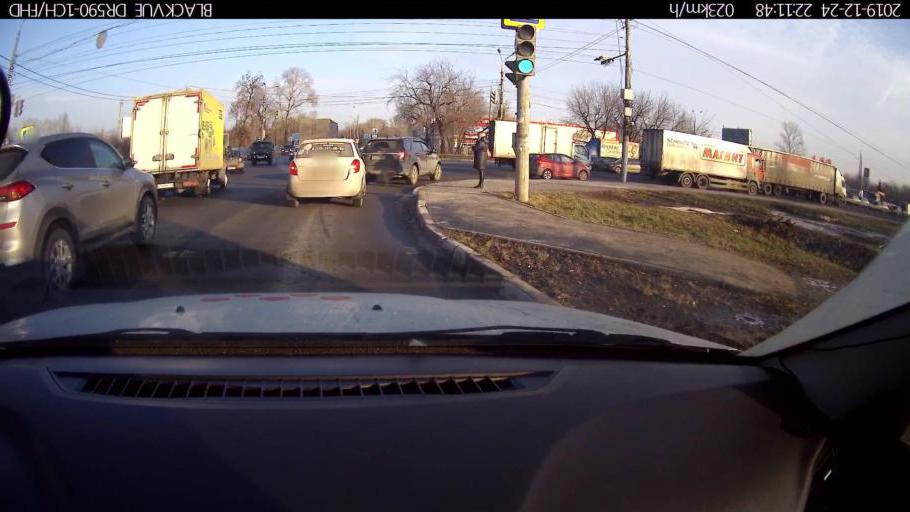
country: RU
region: Nizjnij Novgorod
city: Nizhniy Novgorod
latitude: 56.2581
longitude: 43.9319
